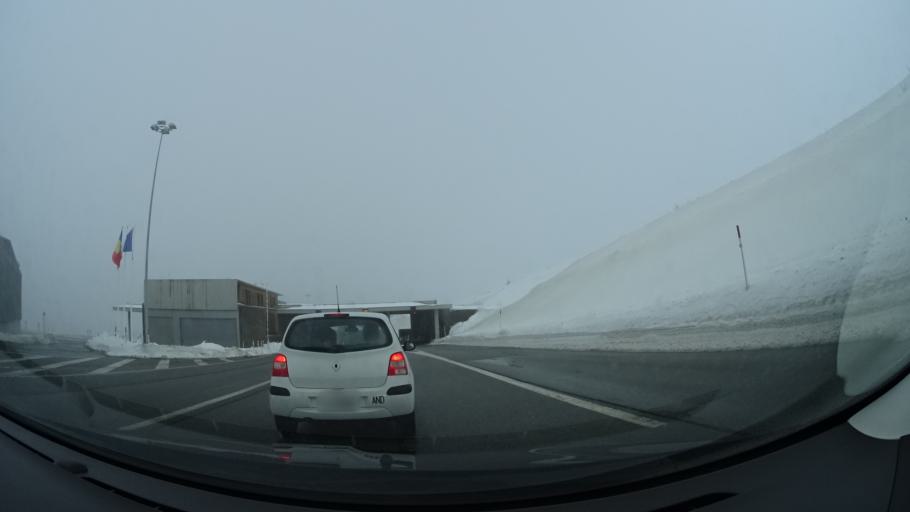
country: AD
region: Encamp
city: Pas de la Casa
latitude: 42.5590
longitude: 1.7555
